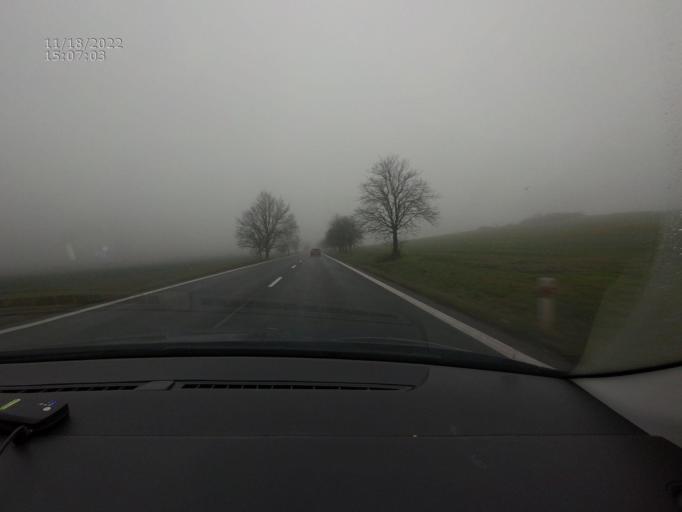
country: CZ
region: Jihocesky
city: Cimelice
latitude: 49.5104
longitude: 14.1043
